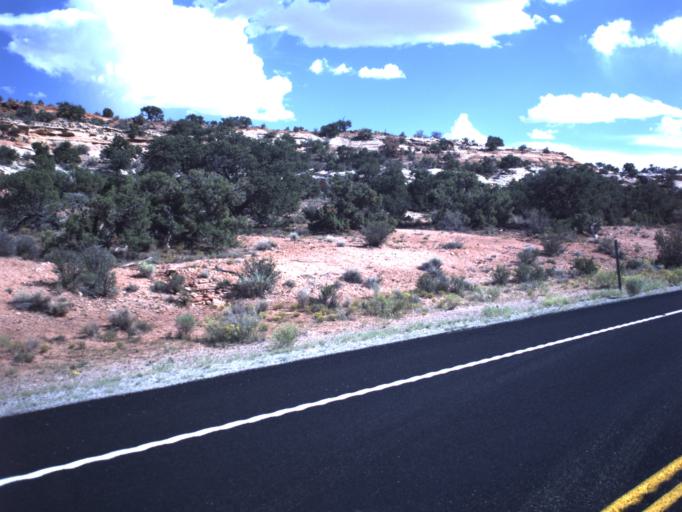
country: US
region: Utah
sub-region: Grand County
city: Moab
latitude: 38.5721
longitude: -109.7922
